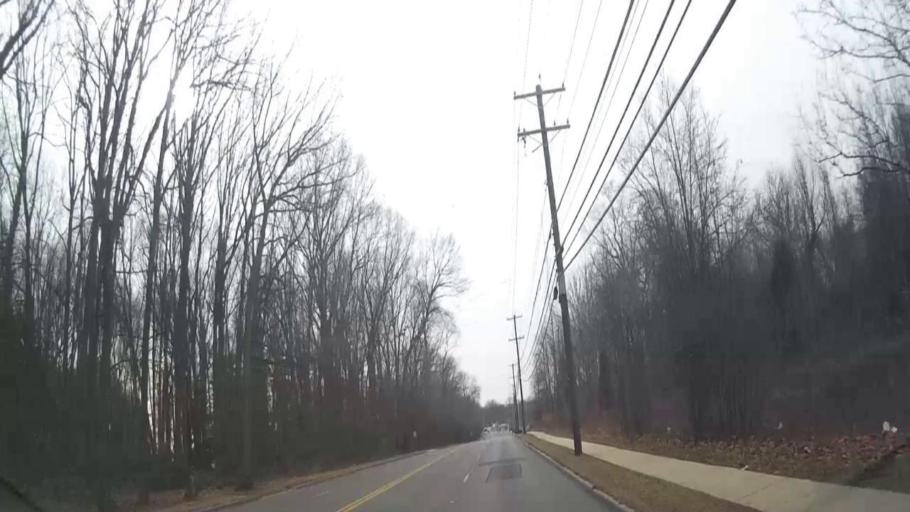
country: US
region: New Jersey
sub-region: Camden County
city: Gibbsboro
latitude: 39.8619
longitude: -74.9701
